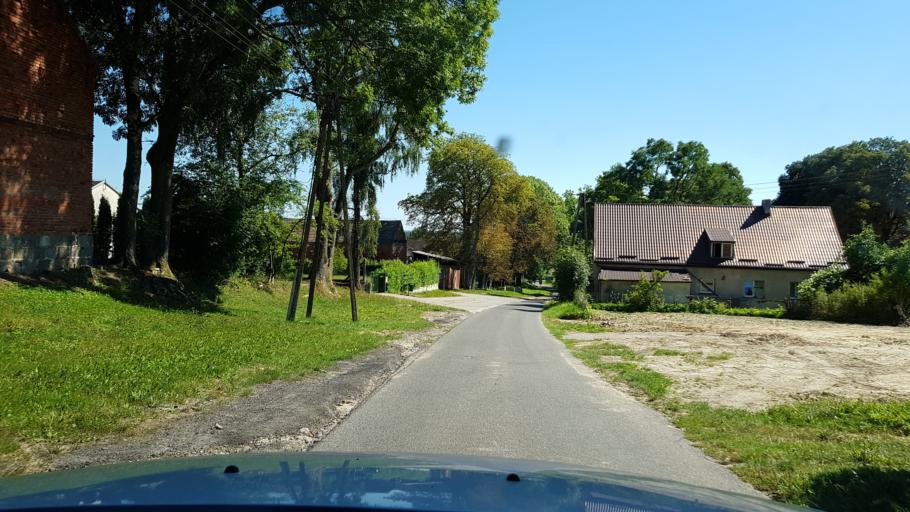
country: PL
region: West Pomeranian Voivodeship
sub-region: Powiat slawienski
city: Darlowo
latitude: 54.4576
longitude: 16.4882
